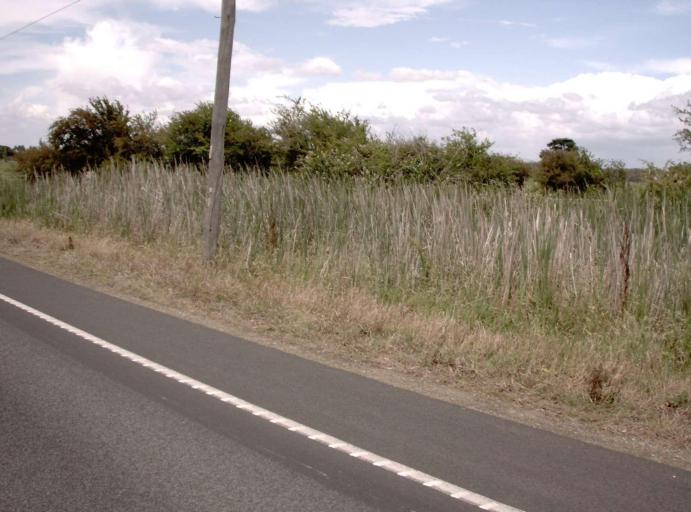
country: AU
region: Victoria
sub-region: Wellington
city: Sale
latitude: -38.0471
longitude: 147.0217
